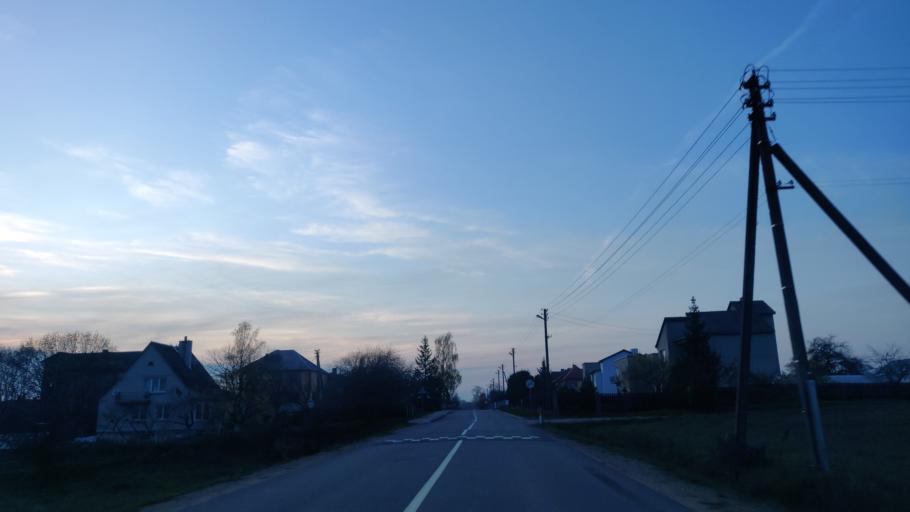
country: LT
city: Trakai
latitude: 54.6098
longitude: 24.9900
